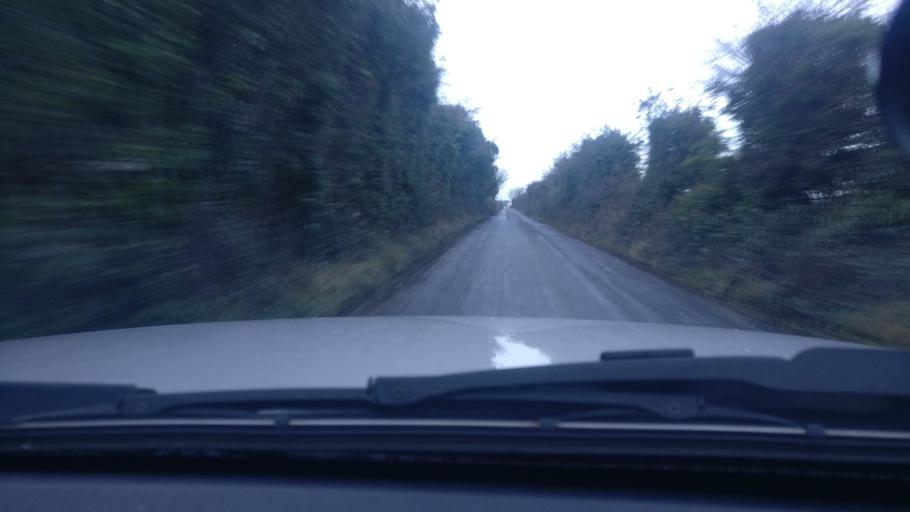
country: IE
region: Connaught
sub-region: County Galway
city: Loughrea
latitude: 53.1956
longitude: -8.5090
